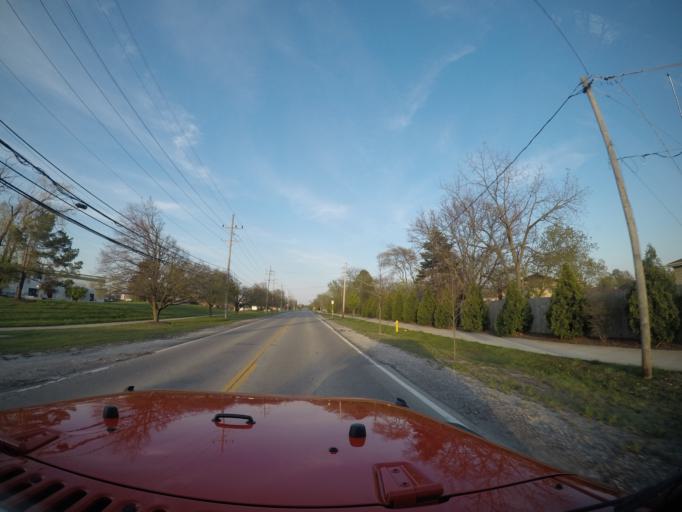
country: US
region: Illinois
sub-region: Cook County
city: Northbrook
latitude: 42.0875
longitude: -87.8439
